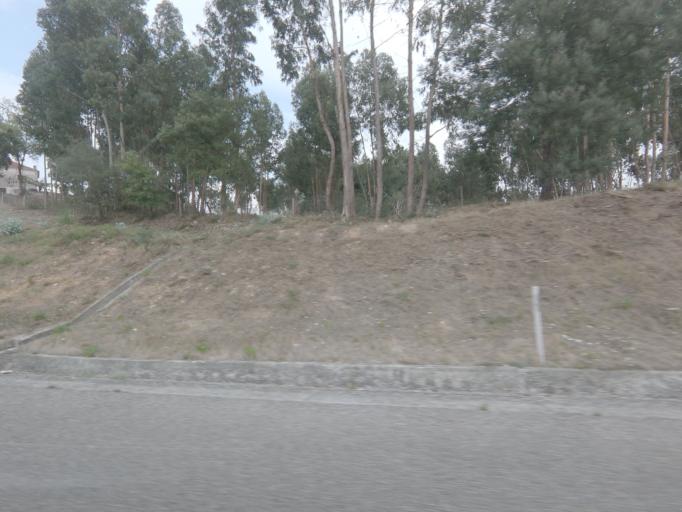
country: PT
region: Coimbra
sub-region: Coimbra
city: Coimbra
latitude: 40.2079
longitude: -8.4472
